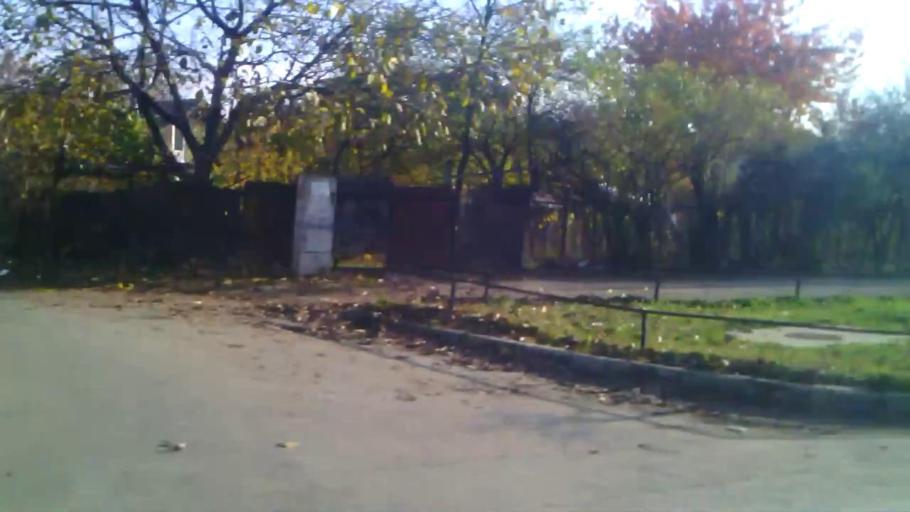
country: RO
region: Ilfov
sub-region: Comuna Popesti-Leordeni
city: Popesti-Leordeni
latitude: 44.3688
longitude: 26.1432
